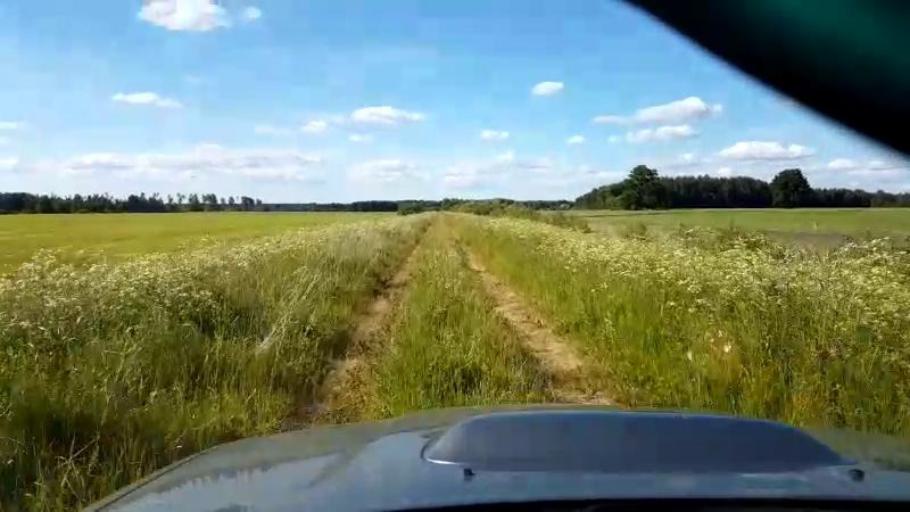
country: EE
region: Paernumaa
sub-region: Sauga vald
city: Sauga
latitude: 58.4974
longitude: 24.5914
